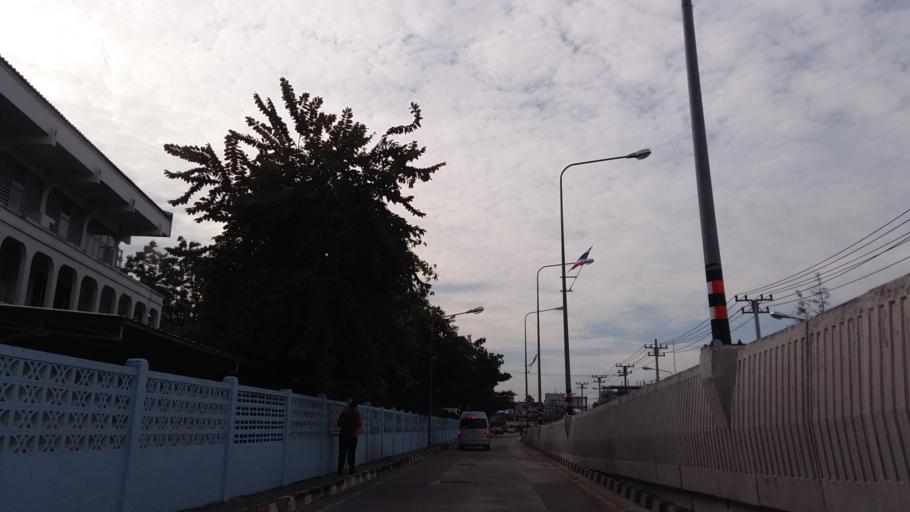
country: TH
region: Chon Buri
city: Chon Buri
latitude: 13.3507
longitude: 100.9779
